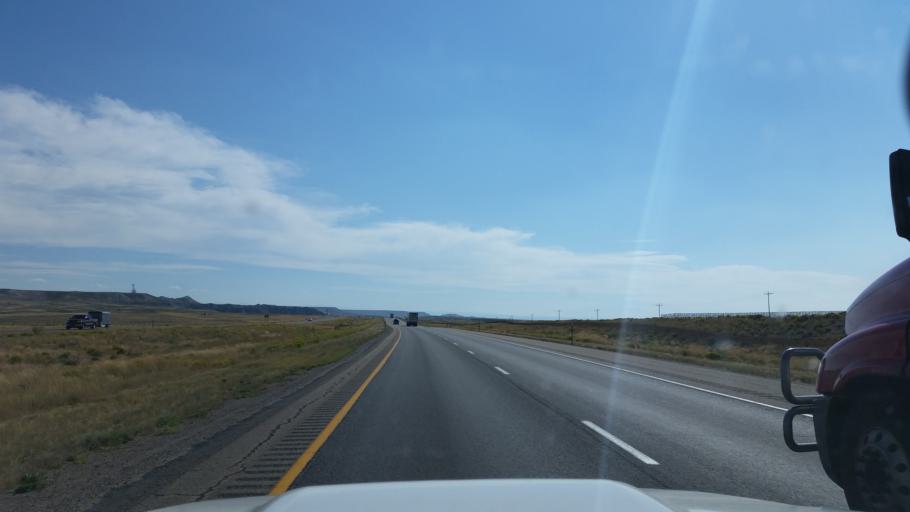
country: US
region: Wyoming
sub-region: Uinta County
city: Lyman
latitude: 41.4891
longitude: -110.0194
